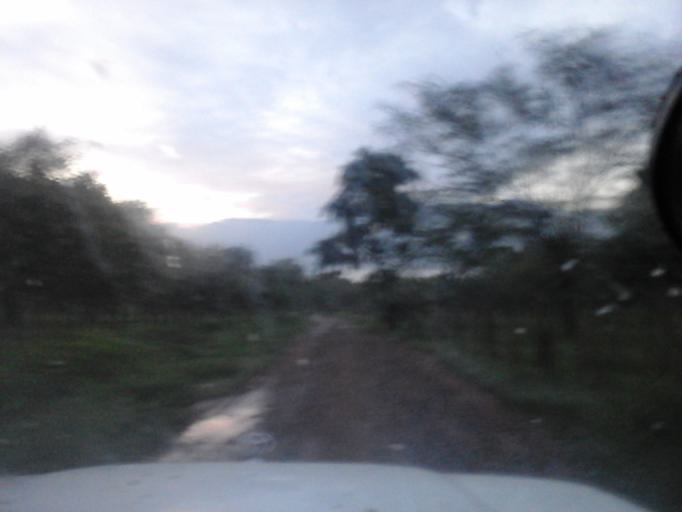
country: CO
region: Cesar
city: Agustin Codazzi
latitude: 10.1557
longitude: -73.2133
